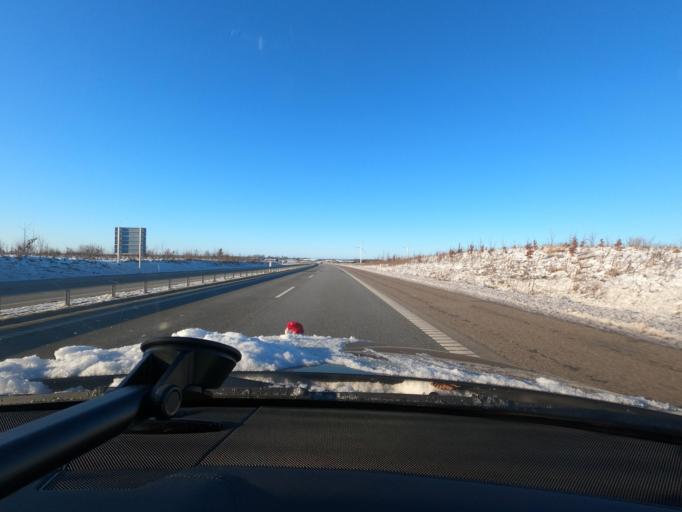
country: DK
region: South Denmark
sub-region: Sonderborg Kommune
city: Dybbol
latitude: 54.9343
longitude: 9.6970
